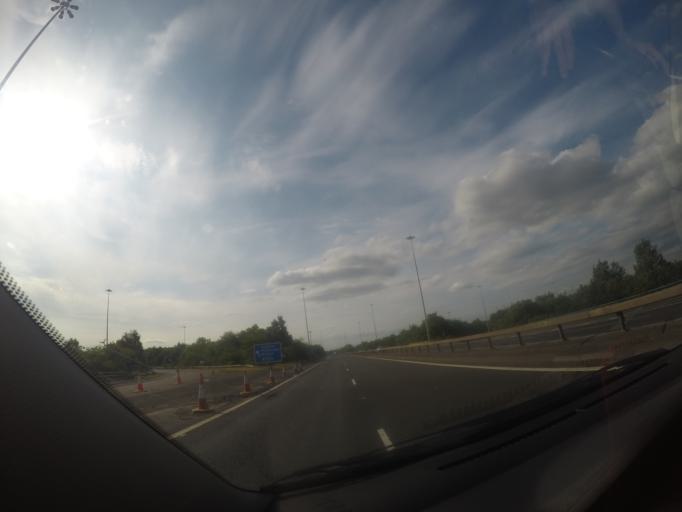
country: GB
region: Scotland
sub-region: South Lanarkshire
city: Hamilton
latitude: 55.7779
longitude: -4.0178
